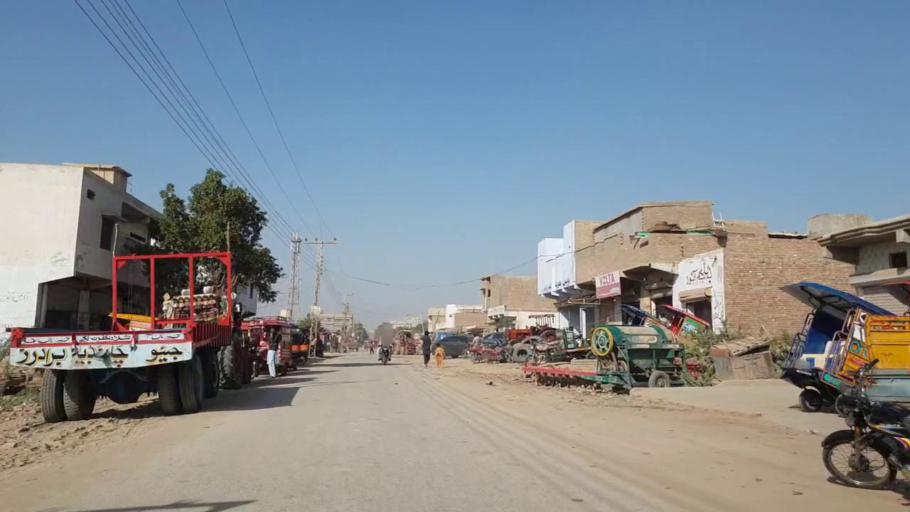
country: PK
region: Sindh
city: Digri
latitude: 25.1498
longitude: 69.1116
